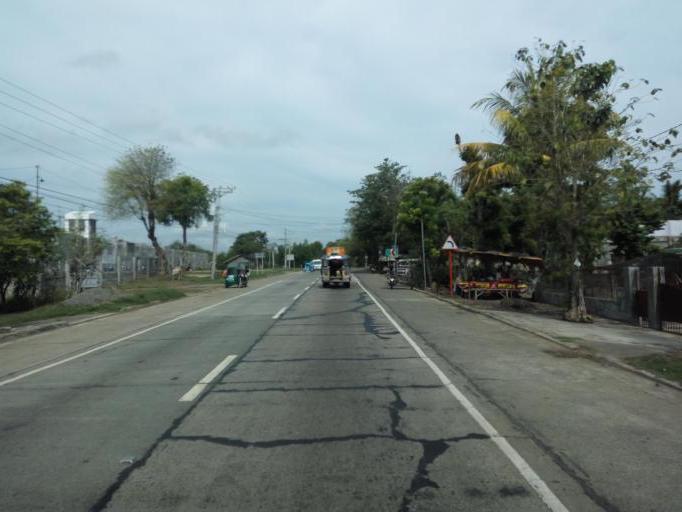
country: PH
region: Cagayan Valley
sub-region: Province of Isabela
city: Reina Mercedes
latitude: 16.9890
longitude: 121.7967
